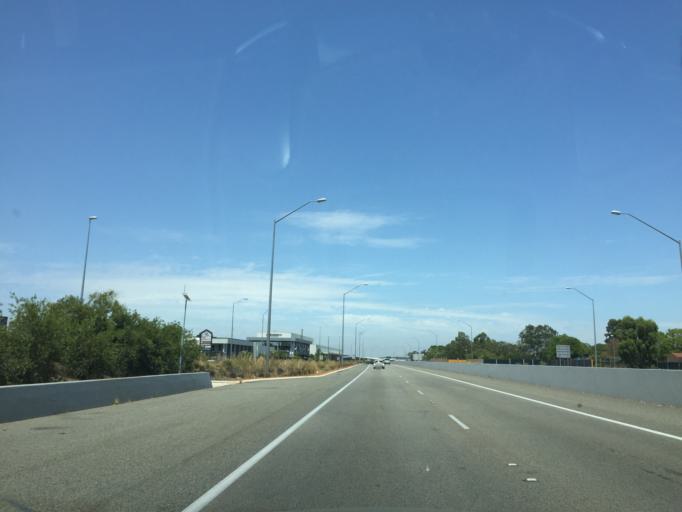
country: AU
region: Western Australia
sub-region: Belmont
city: Kewdale
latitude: -31.9750
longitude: 115.9480
